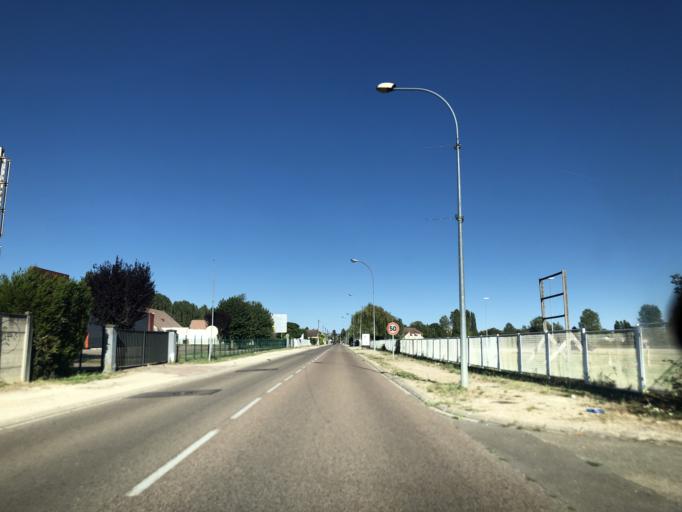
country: FR
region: Bourgogne
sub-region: Departement de l'Yonne
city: Joigny
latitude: 47.9770
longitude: 3.3767
